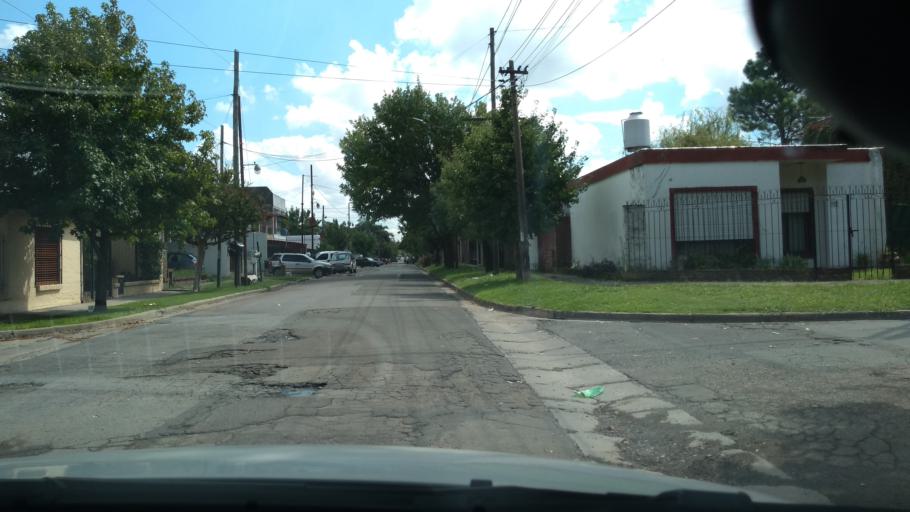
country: AR
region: Buenos Aires
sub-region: Partido de Moron
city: Moron
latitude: -34.6703
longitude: -58.6067
